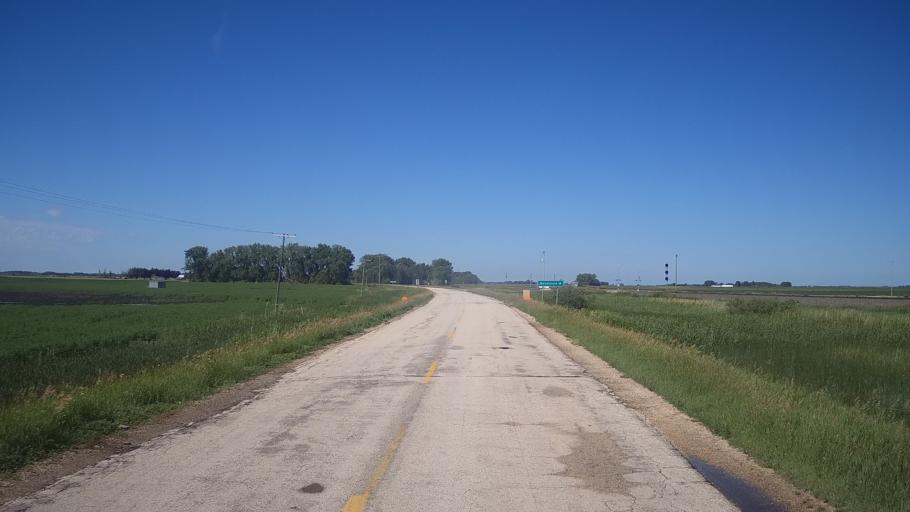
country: CA
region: Manitoba
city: Portage la Prairie
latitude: 50.0420
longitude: -98.0647
